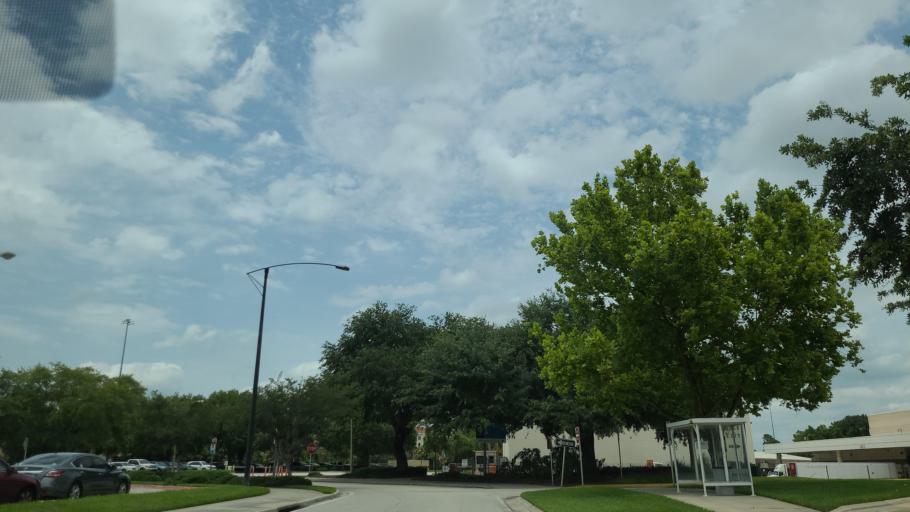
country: US
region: Florida
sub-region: Orange County
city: Williamsburg
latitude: 28.4248
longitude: -81.4722
